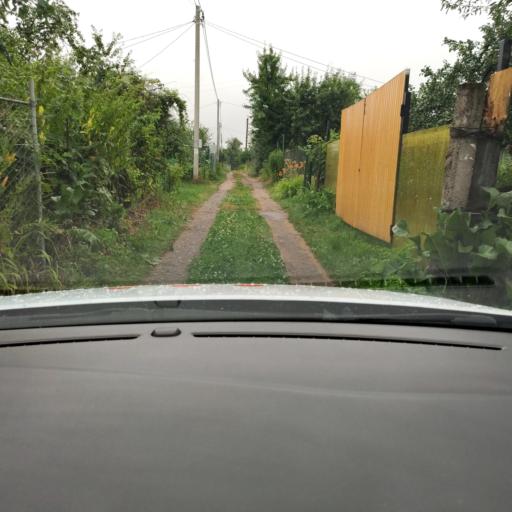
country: RU
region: Tatarstan
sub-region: Gorod Kazan'
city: Kazan
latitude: 55.8525
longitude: 49.0578
